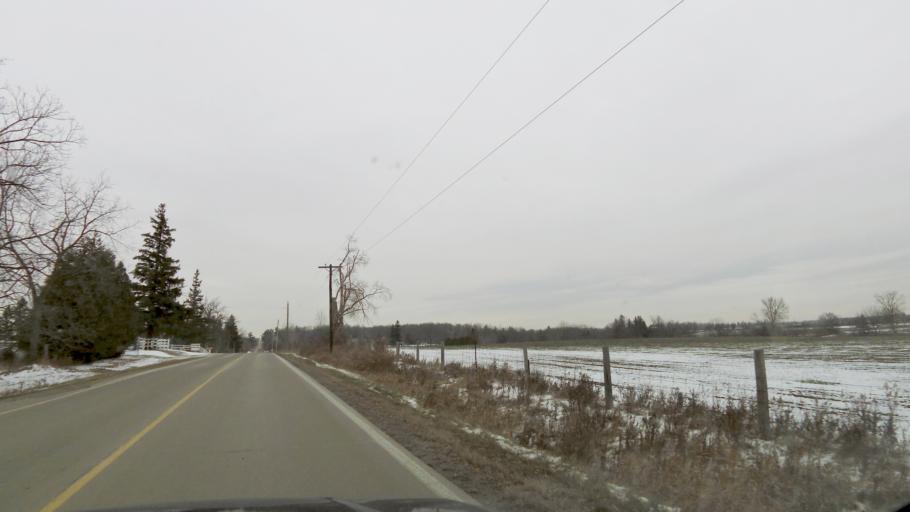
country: CA
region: Ontario
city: Vaughan
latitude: 43.8621
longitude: -79.5915
